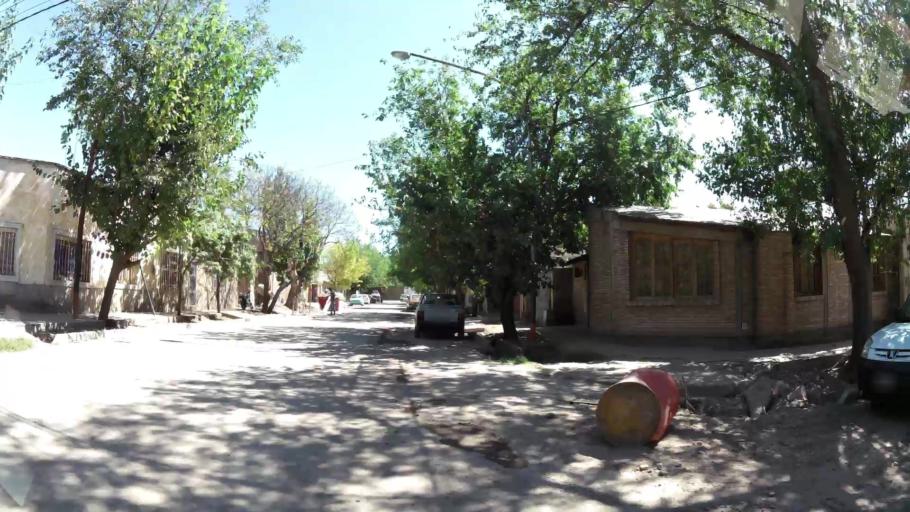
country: AR
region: Mendoza
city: Mendoza
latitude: -32.8815
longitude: -68.8212
